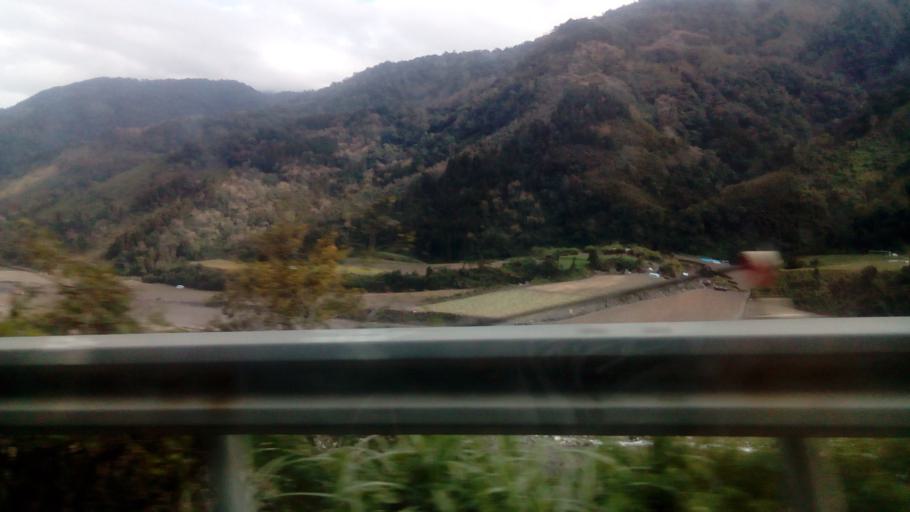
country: TW
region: Taiwan
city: Daxi
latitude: 24.4503
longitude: 121.3895
